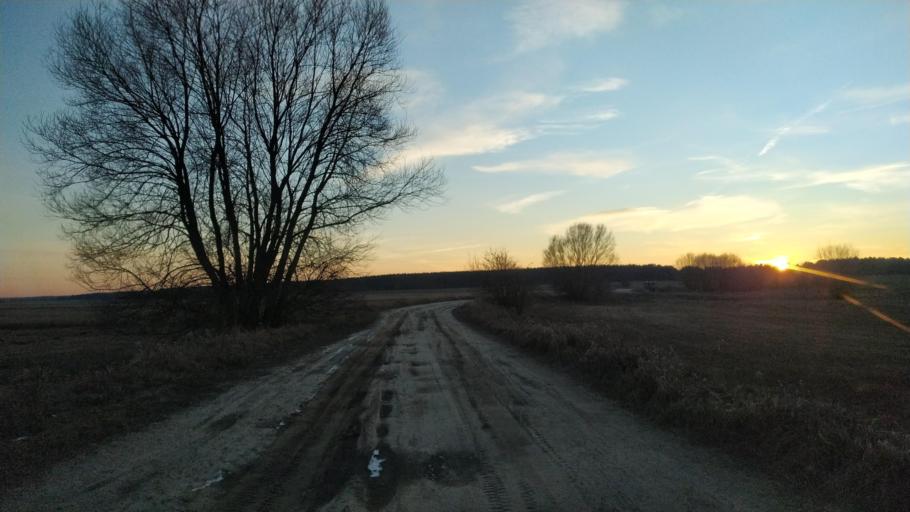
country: BY
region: Brest
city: Pruzhany
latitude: 52.5480
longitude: 24.2494
